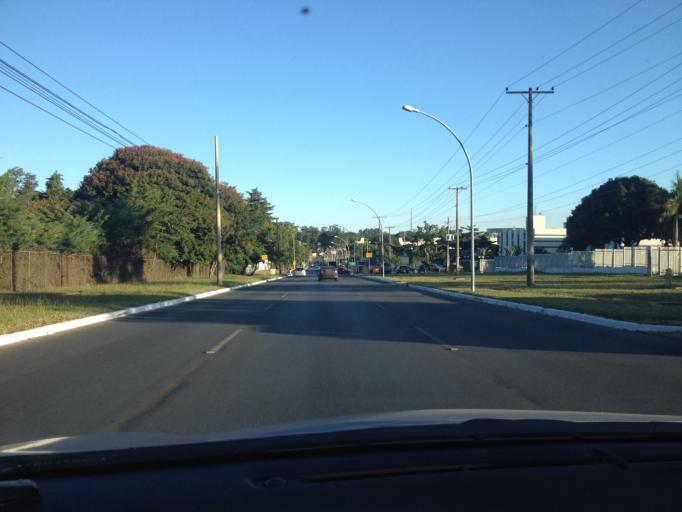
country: BR
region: Federal District
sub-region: Brasilia
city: Brasilia
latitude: -15.7526
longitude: -47.8991
